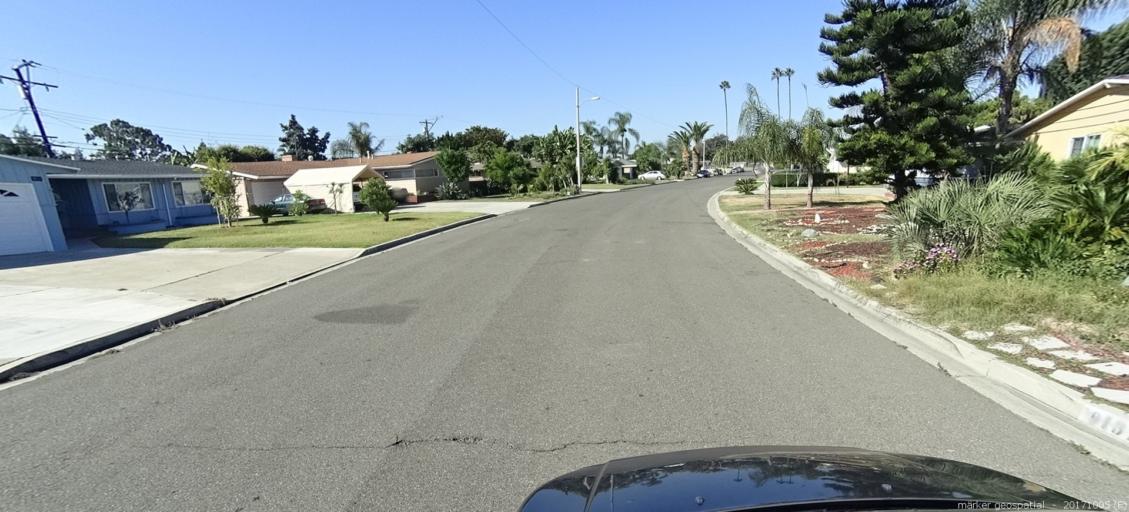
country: US
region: California
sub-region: Orange County
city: Stanton
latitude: 33.7995
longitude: -117.9732
